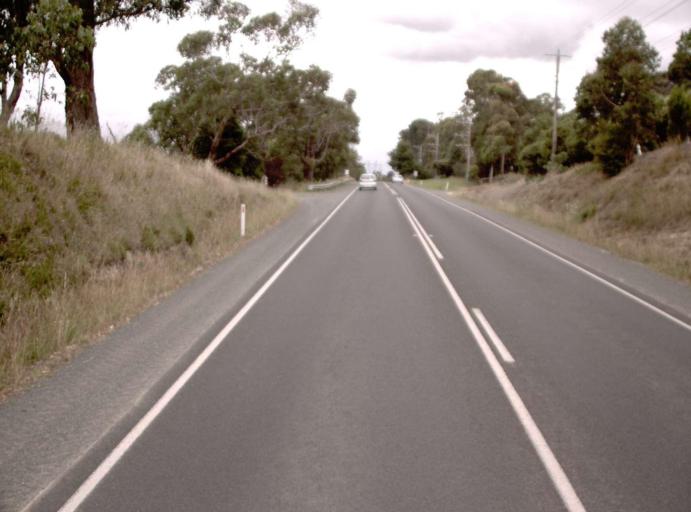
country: AU
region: Victoria
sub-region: Yarra Ranges
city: Woori Yallock
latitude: -37.7756
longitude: 145.4773
